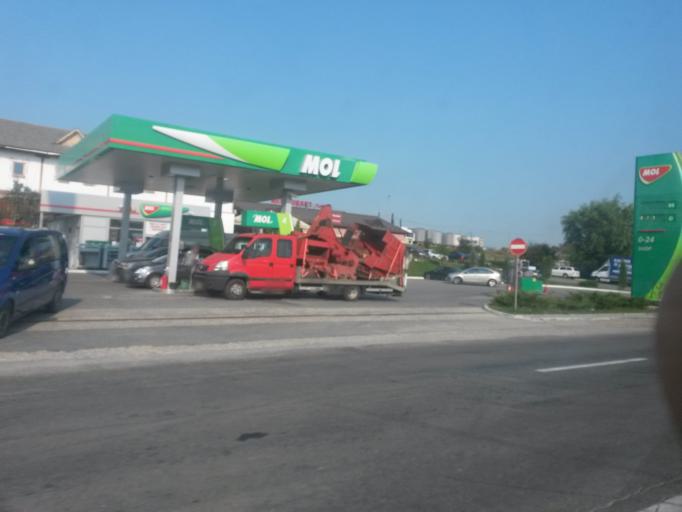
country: RO
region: Cluj
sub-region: Comuna Sandulesti
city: Copaceni
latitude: 46.5873
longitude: 23.7580
